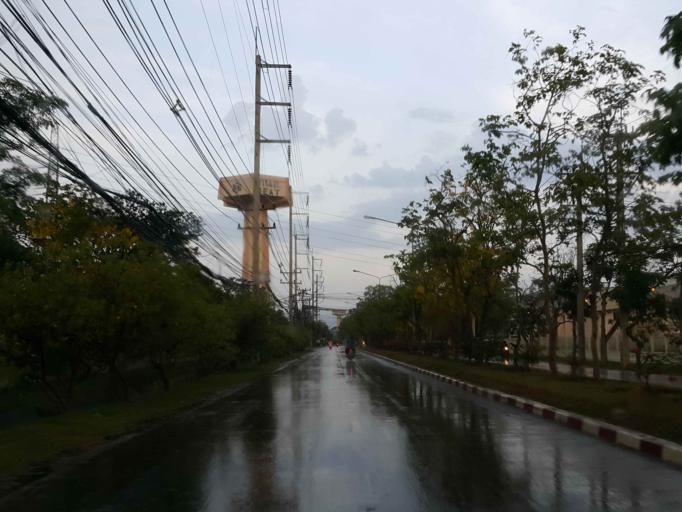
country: TH
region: Lamphun
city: Lamphun
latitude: 18.5893
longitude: 99.0503
